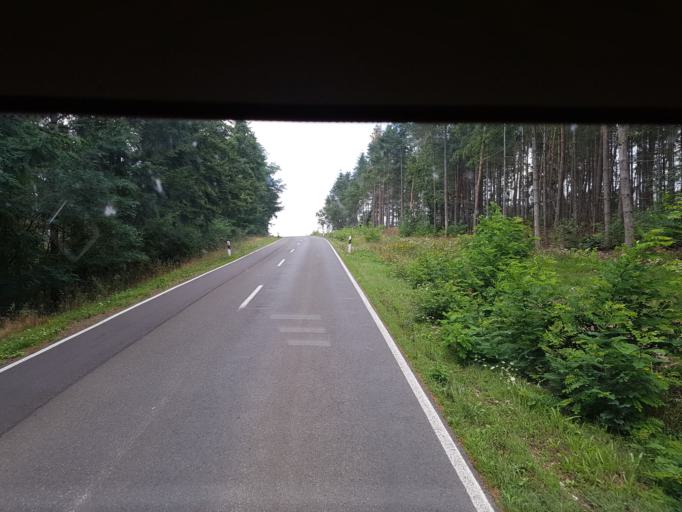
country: DE
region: Rheinland-Pfalz
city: Krov
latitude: 49.9915
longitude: 7.0962
